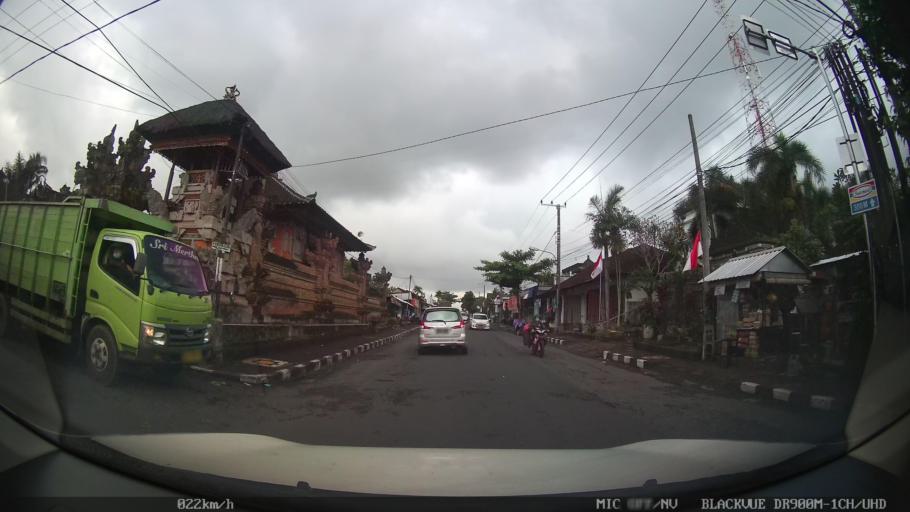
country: ID
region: Bali
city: Banjar Sempidi
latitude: -8.5176
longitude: 115.2098
